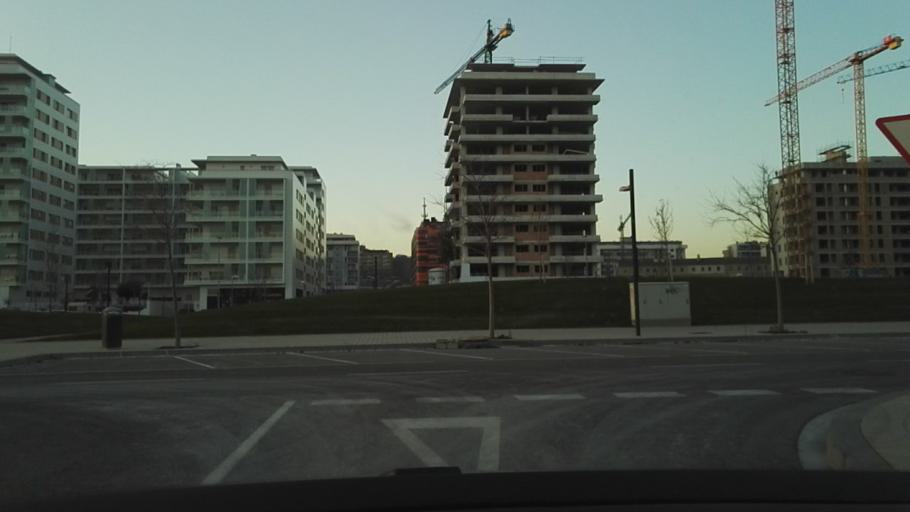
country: ES
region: Navarre
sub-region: Provincia de Navarra
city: Segundo Ensanche
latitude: 42.8059
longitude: -1.6269
